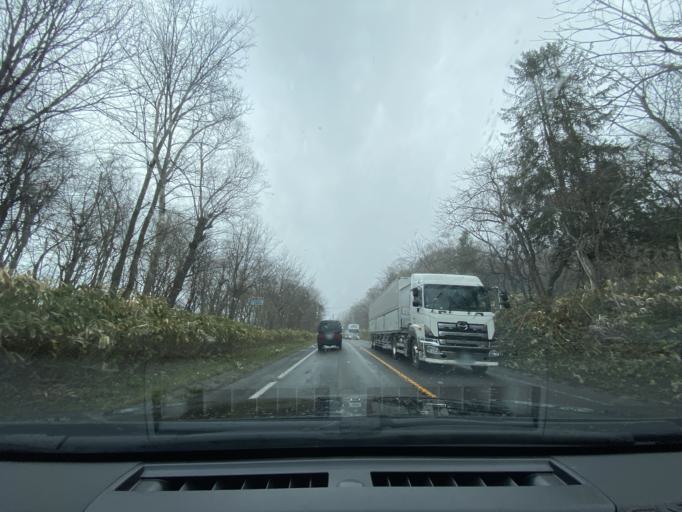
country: JP
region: Hokkaido
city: Fukagawa
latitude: 43.7061
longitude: 142.1056
